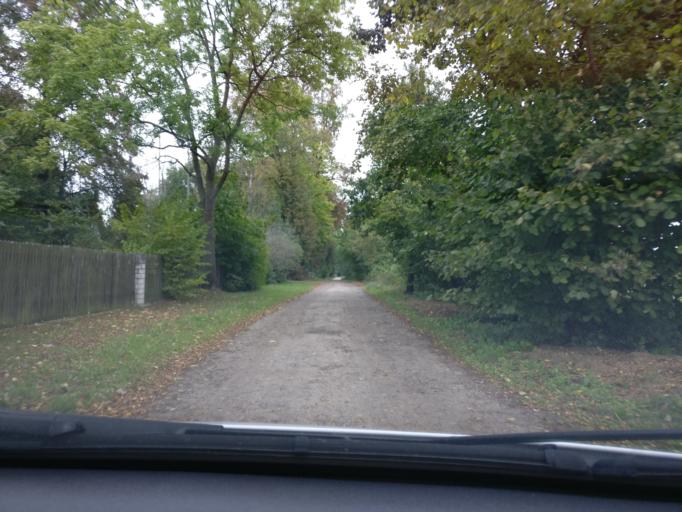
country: PL
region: Masovian Voivodeship
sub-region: Powiat kozienicki
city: Garbatka-Letnisko
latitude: 51.5123
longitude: 21.5984
